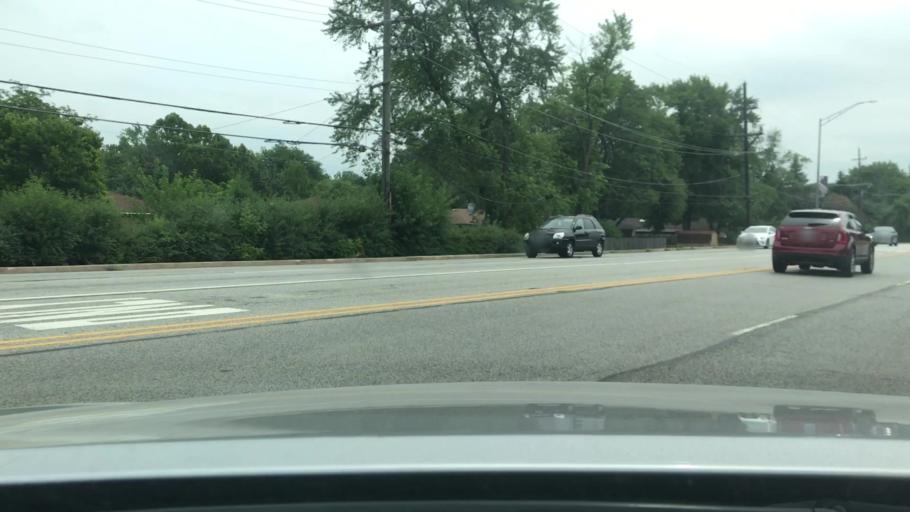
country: US
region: Illinois
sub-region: DuPage County
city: Darien
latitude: 41.7493
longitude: -87.9739
